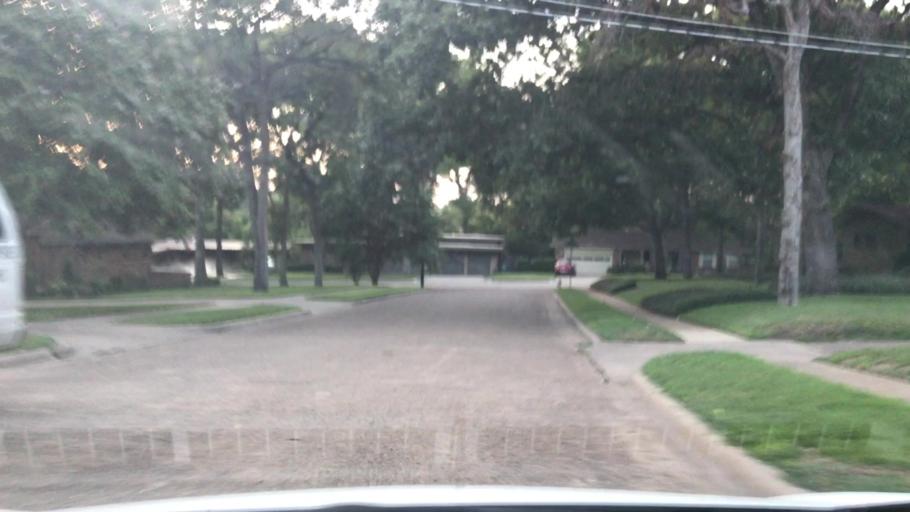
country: US
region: Texas
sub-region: Dallas County
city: Highland Park
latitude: 32.8625
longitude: -96.7133
